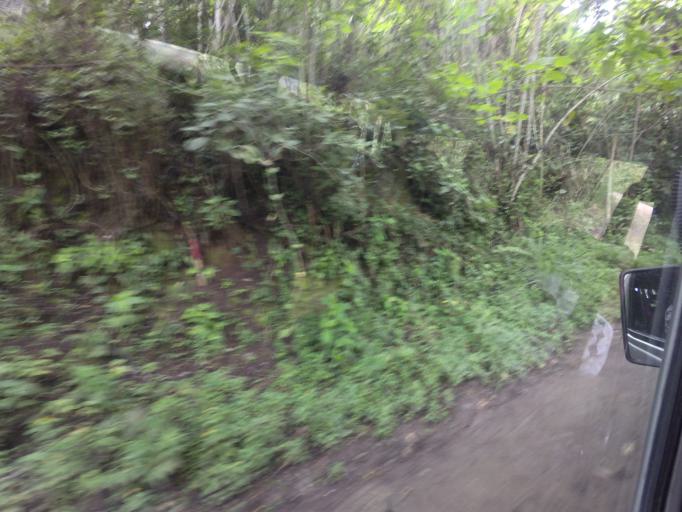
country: CO
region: Huila
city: San Agustin
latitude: 1.9222
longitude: -76.2964
